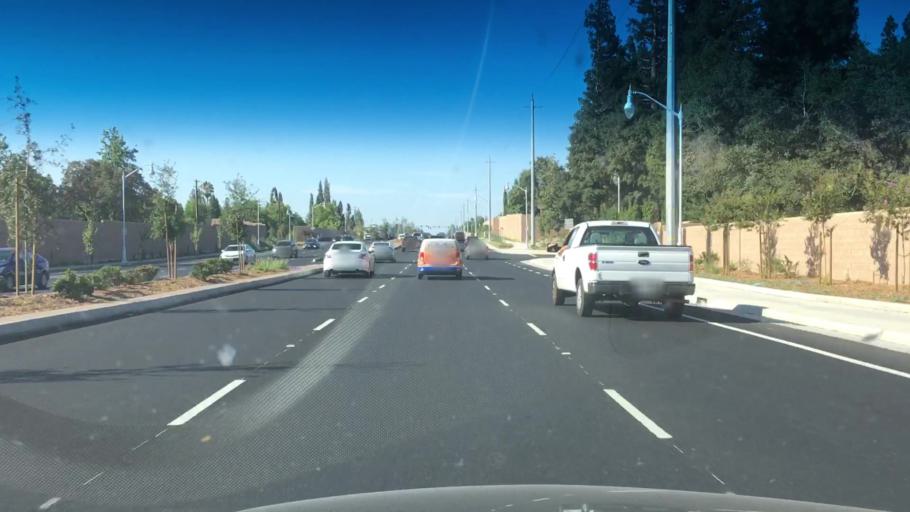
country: US
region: California
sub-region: Sacramento County
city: Gold River
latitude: 38.6414
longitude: -121.2254
